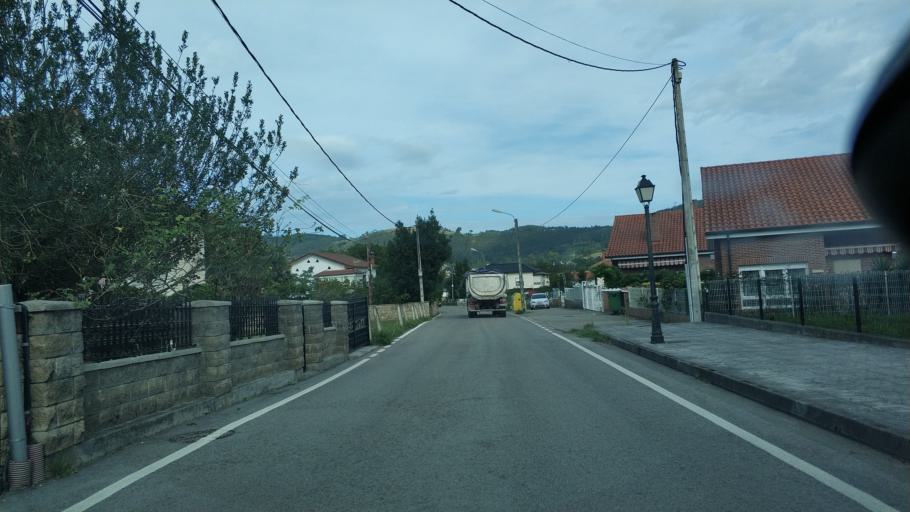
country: ES
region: Cantabria
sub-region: Provincia de Cantabria
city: Santa Maria de Cayon
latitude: 43.3089
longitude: -3.8767
